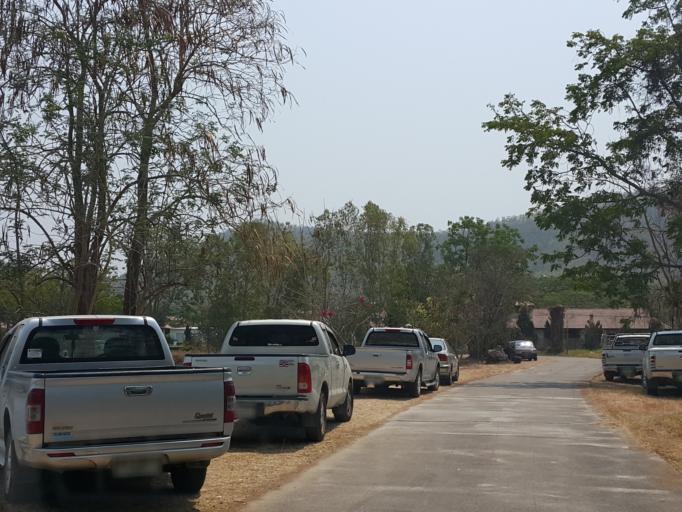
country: TH
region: Chiang Mai
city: San Kamphaeng
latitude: 18.7167
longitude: 99.1790
